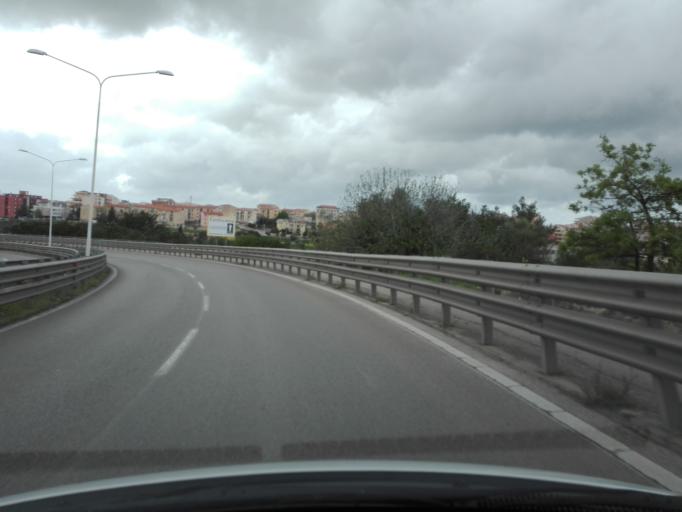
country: IT
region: Sardinia
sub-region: Provincia di Sassari
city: Sassari
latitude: 40.7312
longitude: 8.5763
